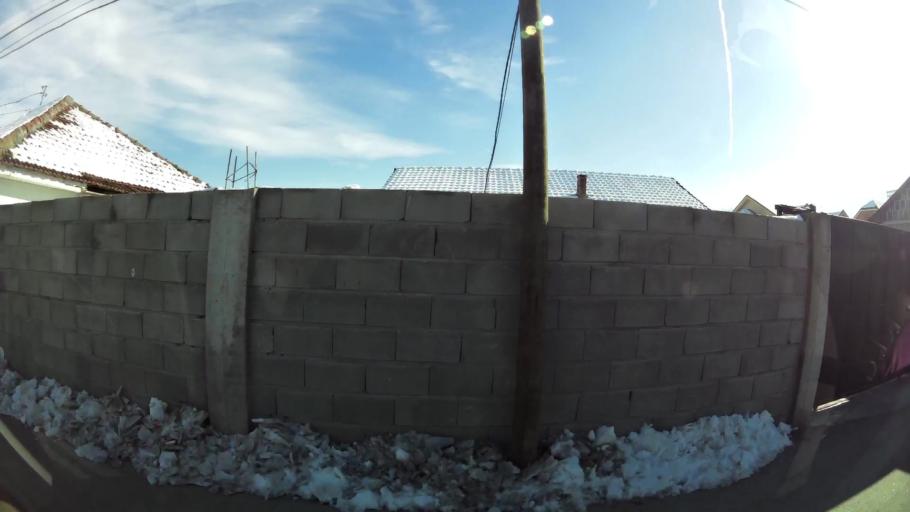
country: MK
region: Saraj
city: Saraj
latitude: 41.9982
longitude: 21.3187
